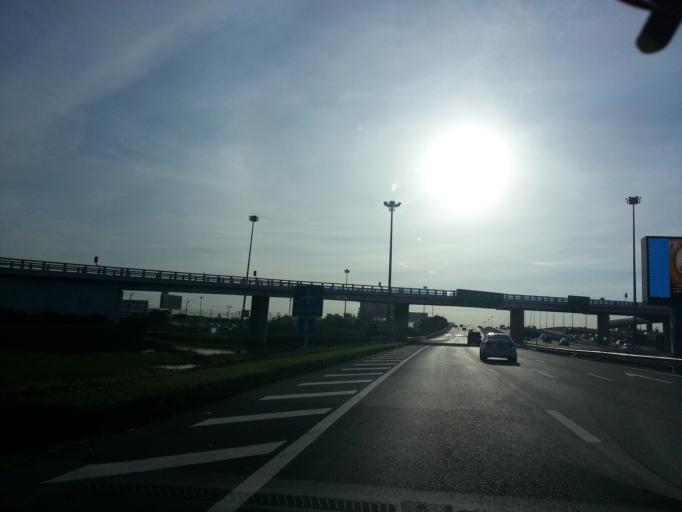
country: TH
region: Bangkok
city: Lat Krabang
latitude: 13.7298
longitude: 100.7427
